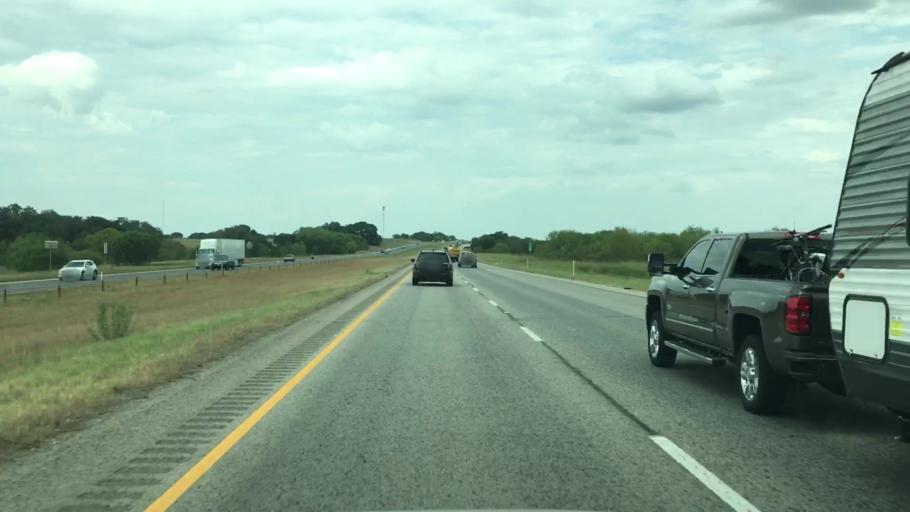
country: US
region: Texas
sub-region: Atascosa County
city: Pleasanton
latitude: 29.1114
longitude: -98.4320
